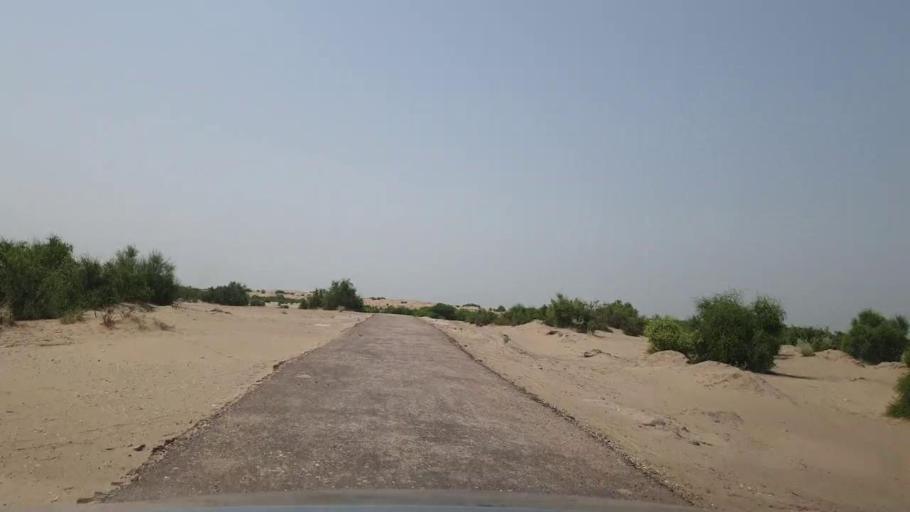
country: PK
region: Sindh
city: Pano Aqil
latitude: 27.6051
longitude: 69.1467
